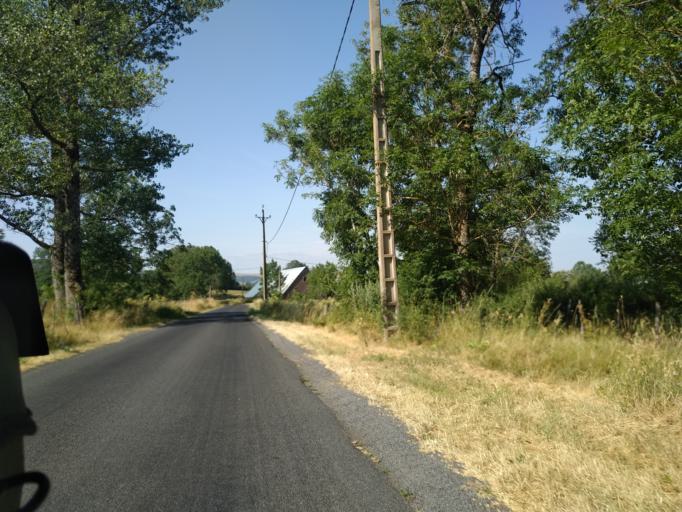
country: FR
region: Auvergne
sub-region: Departement du Cantal
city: Riom-es-Montagnes
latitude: 45.2428
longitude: 2.7402
